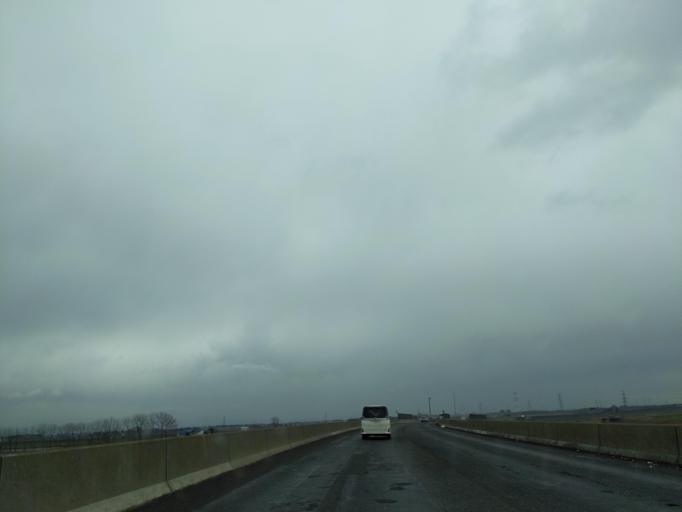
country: JP
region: Hokkaido
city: Tobetsu
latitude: 43.1845
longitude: 141.5569
